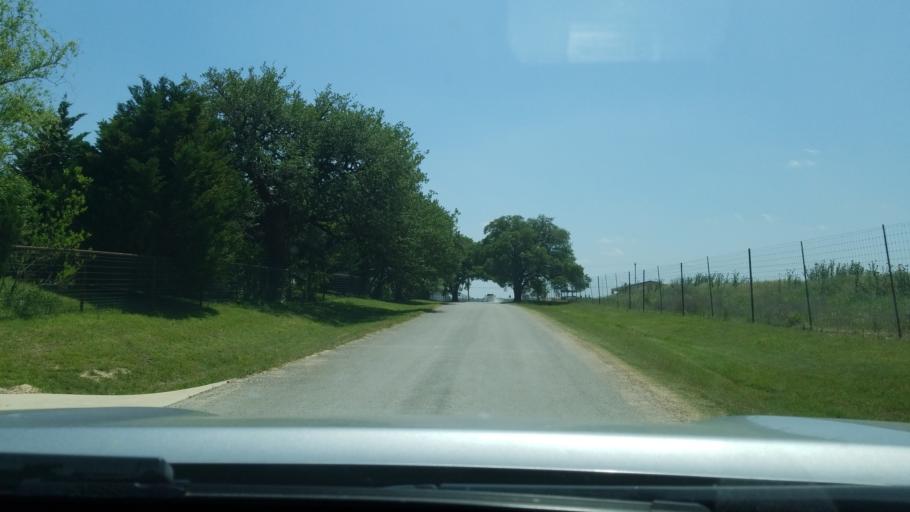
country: US
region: Texas
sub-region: Blanco County
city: Blanco
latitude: 30.0701
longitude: -98.3985
